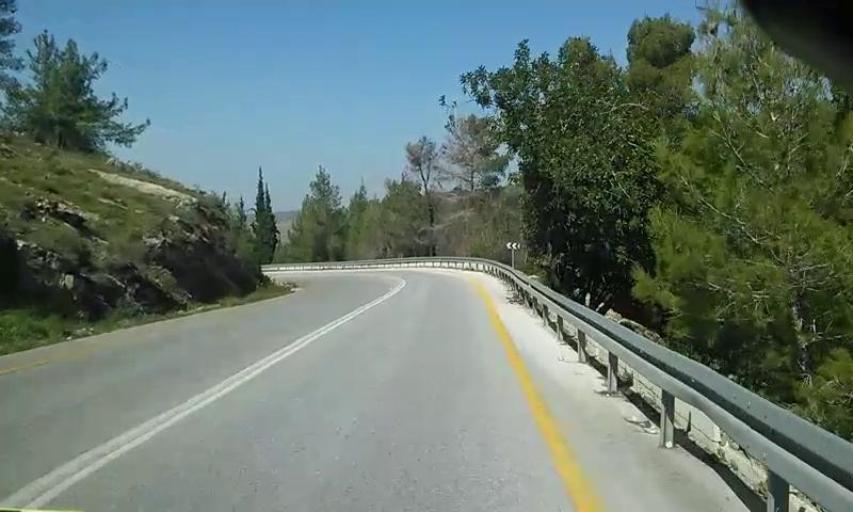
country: PS
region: West Bank
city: Nahhalin
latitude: 31.6734
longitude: 35.1038
